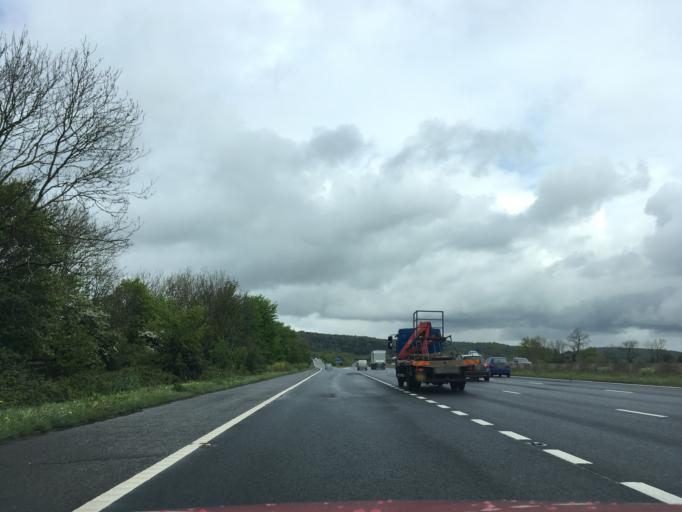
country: GB
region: England
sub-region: North Somerset
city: Kenn
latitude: 51.4268
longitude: -2.8434
